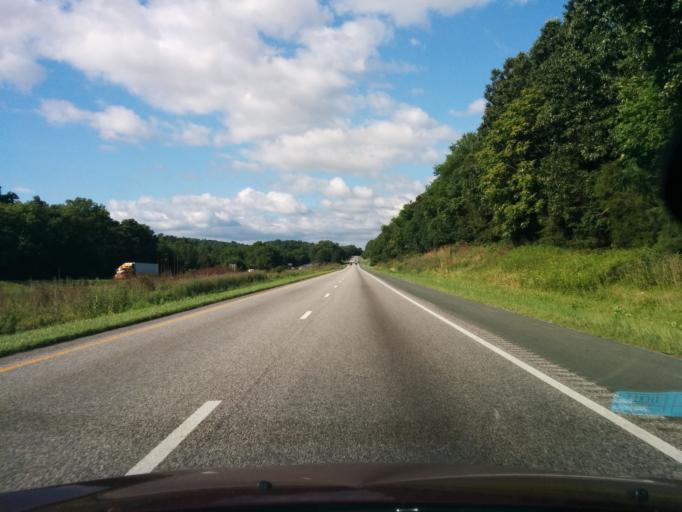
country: US
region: Virginia
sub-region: City of Lexington
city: Lexington
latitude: 37.7328
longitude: -79.4291
